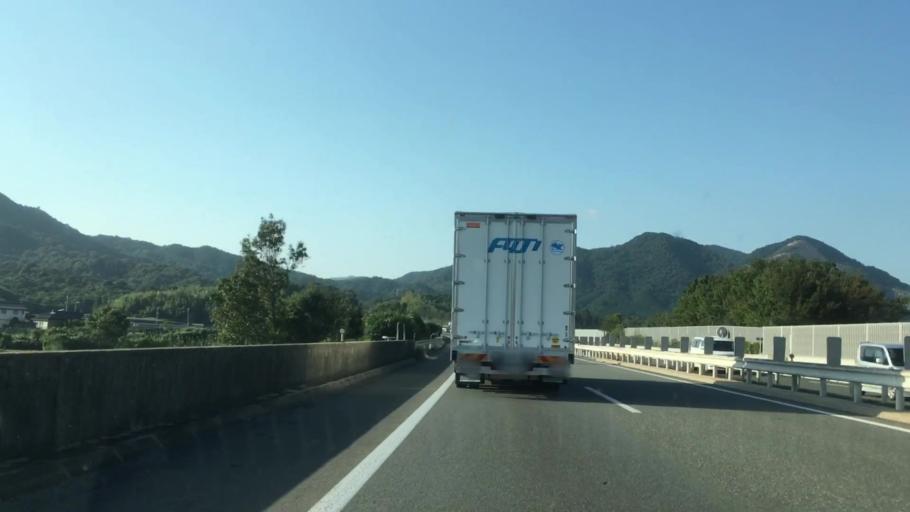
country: JP
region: Yamaguchi
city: Hofu
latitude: 34.0698
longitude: 131.4984
